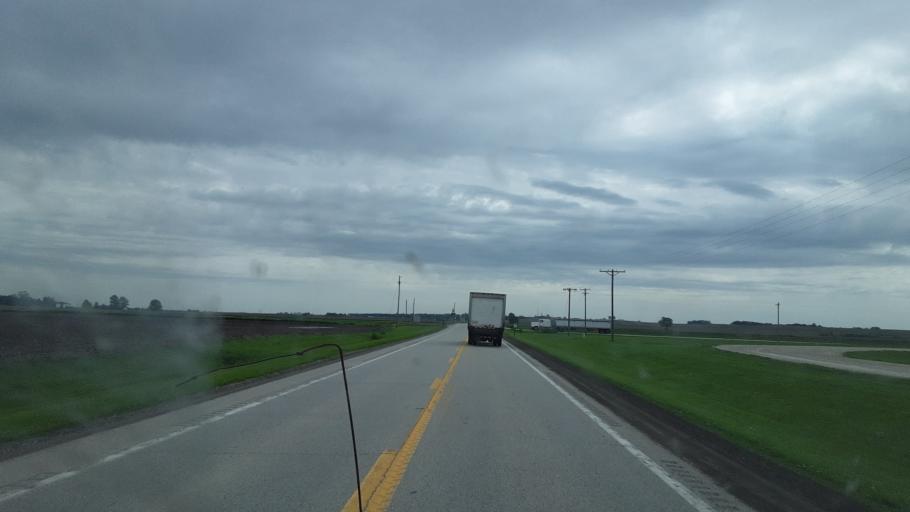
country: US
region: Illinois
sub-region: Mason County
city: Mason City
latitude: 40.3051
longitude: -89.6529
